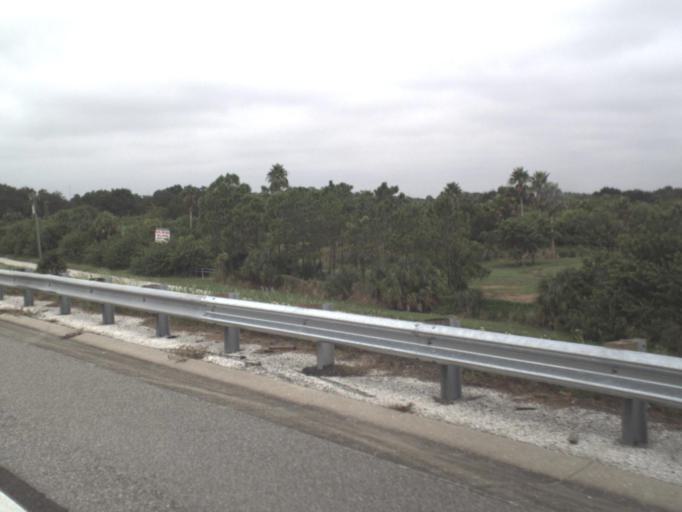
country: US
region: Florida
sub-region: Manatee County
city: Memphis
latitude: 27.5807
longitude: -82.5675
